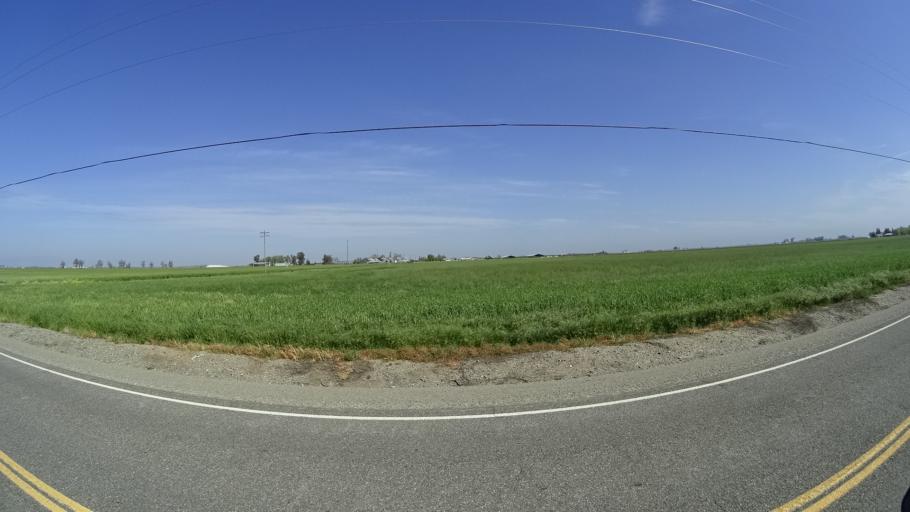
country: US
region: California
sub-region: Glenn County
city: Willows
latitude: 39.5828
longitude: -122.0881
